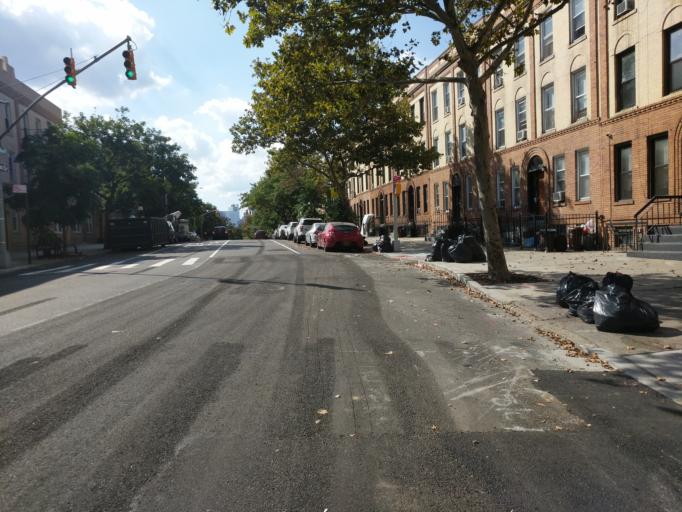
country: US
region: New York
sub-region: Queens County
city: Long Island City
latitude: 40.7457
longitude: -73.9102
